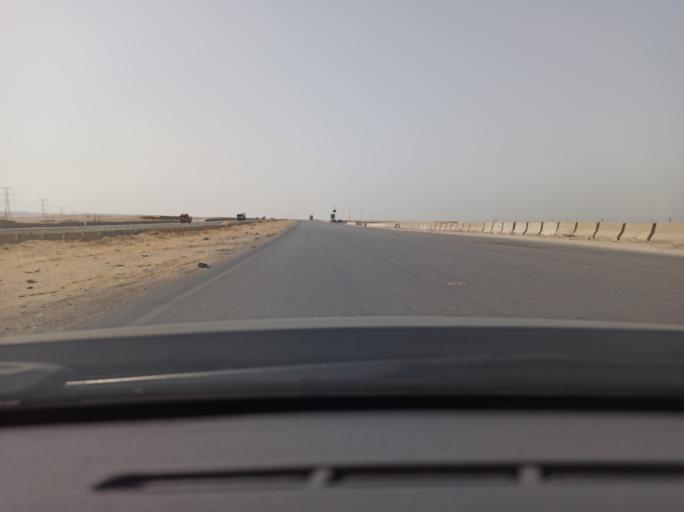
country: EG
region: Muhafazat al Fayyum
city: Al Wasitah
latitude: 29.3807
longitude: 31.3132
